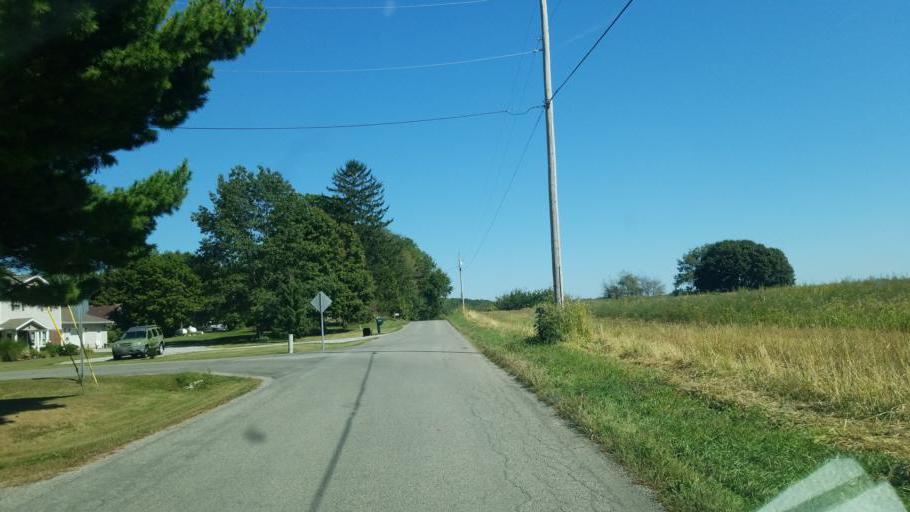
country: US
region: Ohio
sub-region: Logan County
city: West Liberty
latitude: 40.3052
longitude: -83.7296
